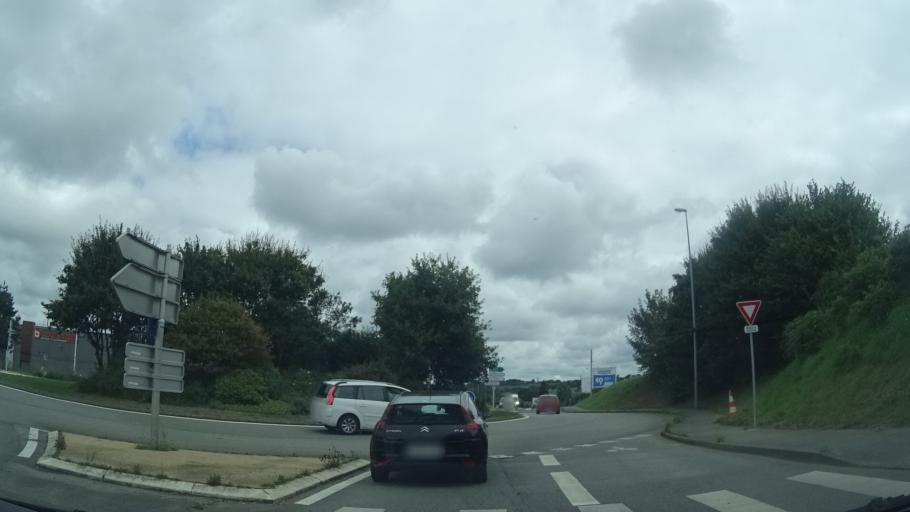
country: FR
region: Brittany
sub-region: Departement du Finistere
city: Le Relecq-Kerhuon
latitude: 48.4146
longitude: -4.4382
